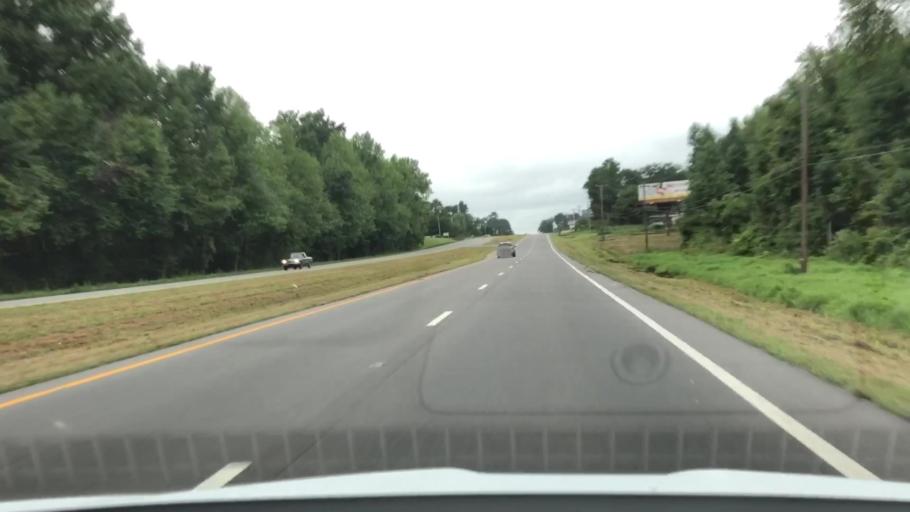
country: US
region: North Carolina
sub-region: Lenoir County
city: La Grange
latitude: 35.2745
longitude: -77.7444
